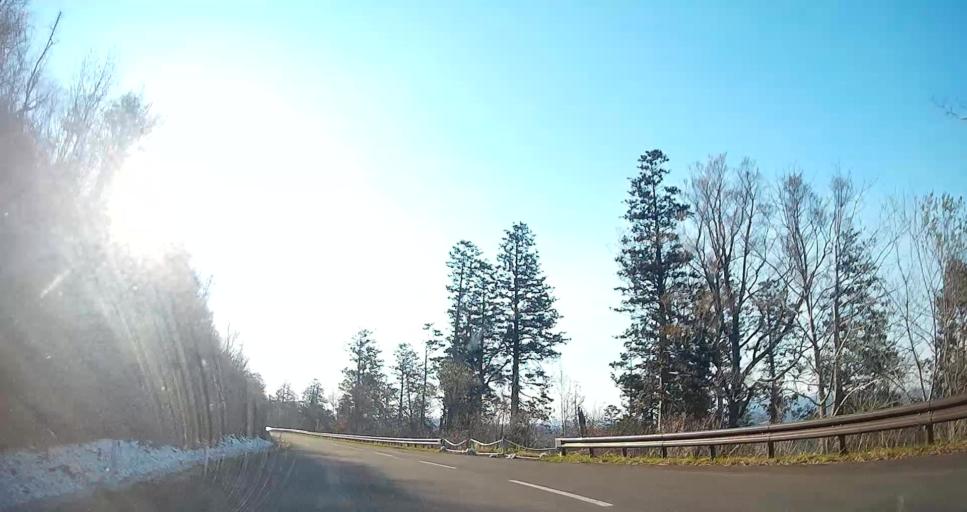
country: JP
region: Aomori
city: Mutsu
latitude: 41.3118
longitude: 141.1128
